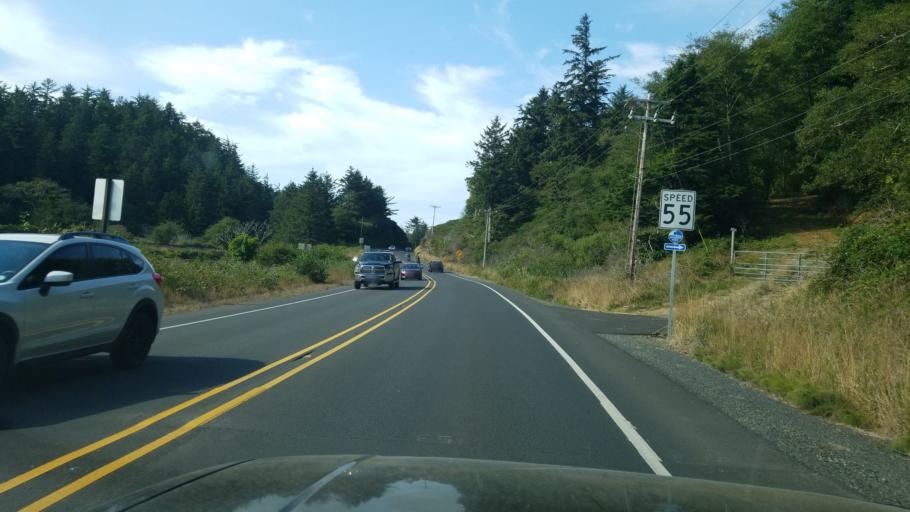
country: US
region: Oregon
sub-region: Tillamook County
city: Rockaway Beach
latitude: 45.5711
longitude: -123.9428
